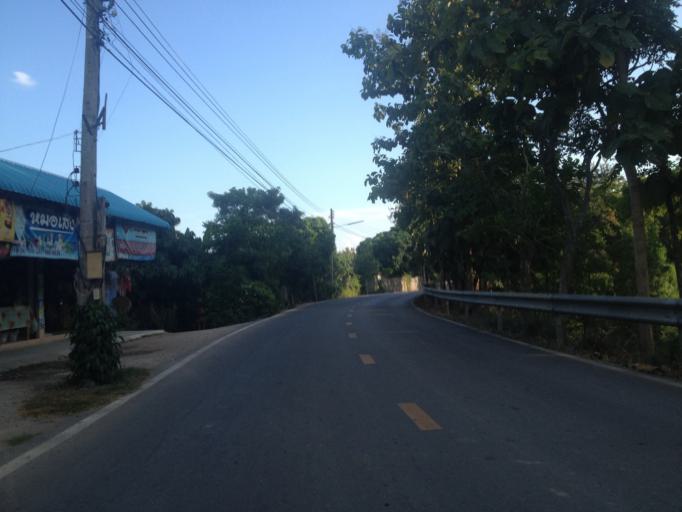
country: TH
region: Chiang Mai
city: San Pa Tong
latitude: 18.6031
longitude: 98.8594
